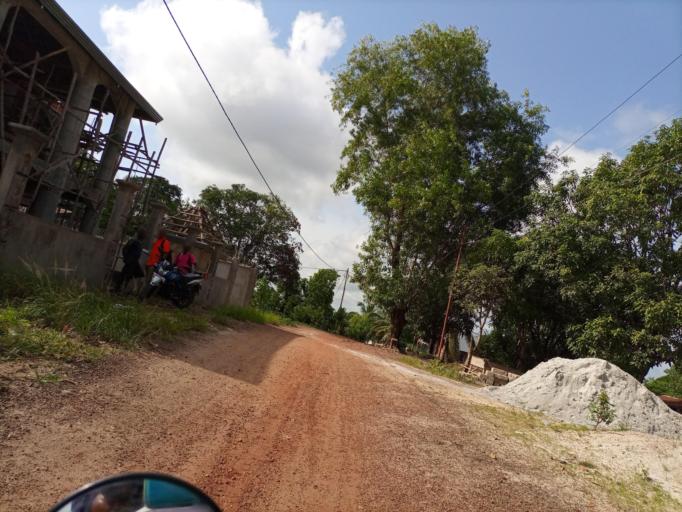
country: SL
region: Southern Province
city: Bo
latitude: 7.9608
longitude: -11.7640
